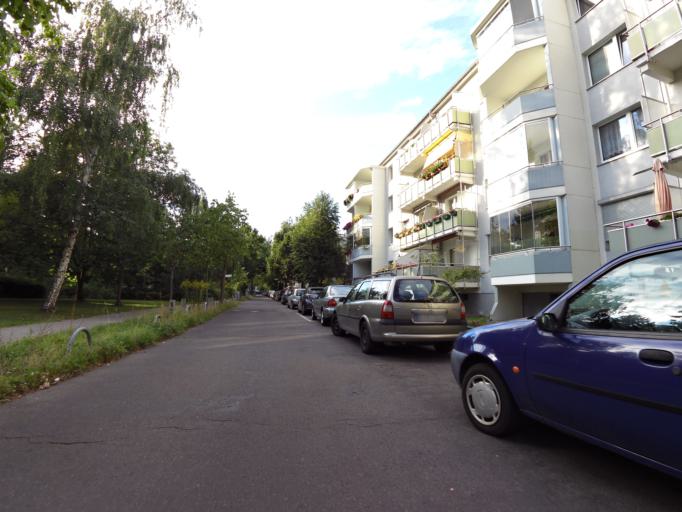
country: DE
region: Berlin
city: Baumschulenweg
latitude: 52.4676
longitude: 13.4807
